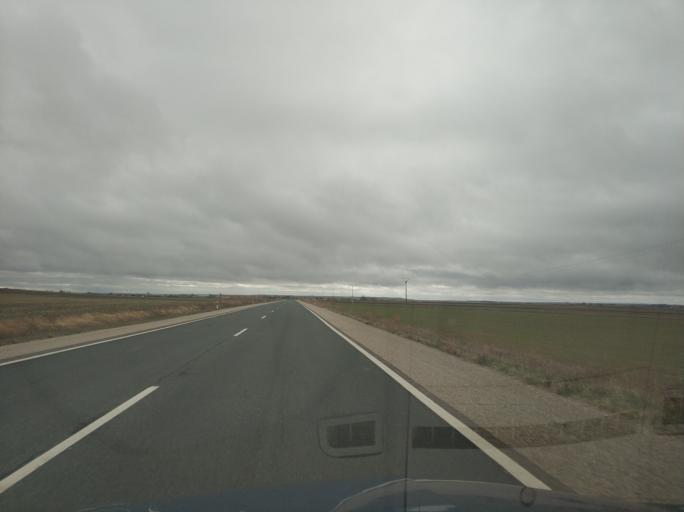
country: ES
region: Castille and Leon
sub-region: Provincia de Salamanca
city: Villaverde de Guarena
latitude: 41.0760
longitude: -5.5273
